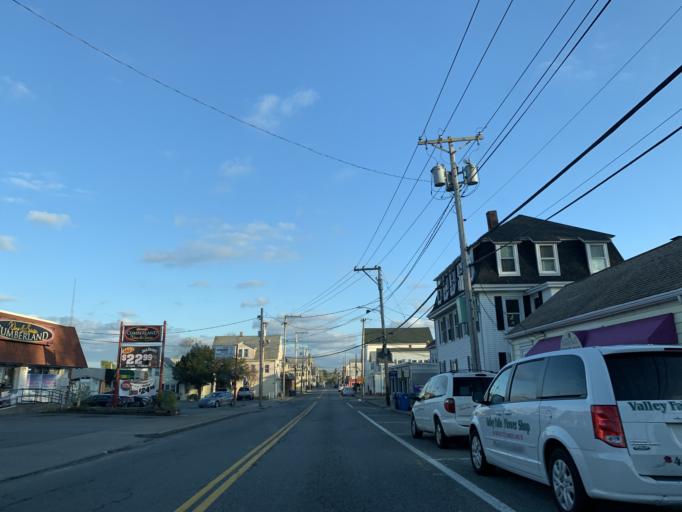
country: US
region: Rhode Island
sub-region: Providence County
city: Valley Falls
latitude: 41.9055
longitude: -71.3926
